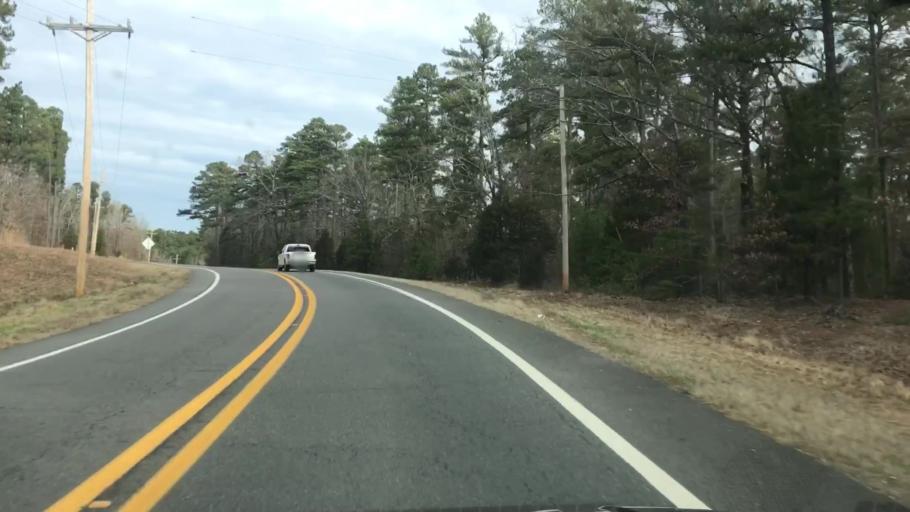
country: US
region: Arkansas
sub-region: Montgomery County
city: Mount Ida
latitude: 34.5876
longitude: -93.6634
